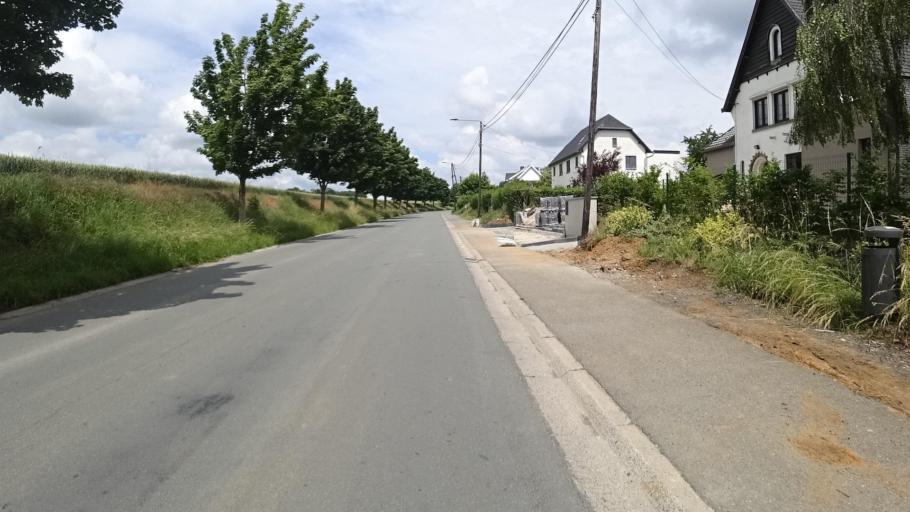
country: BE
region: Wallonia
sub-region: Province de Namur
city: Namur
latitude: 50.4794
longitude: 4.8636
